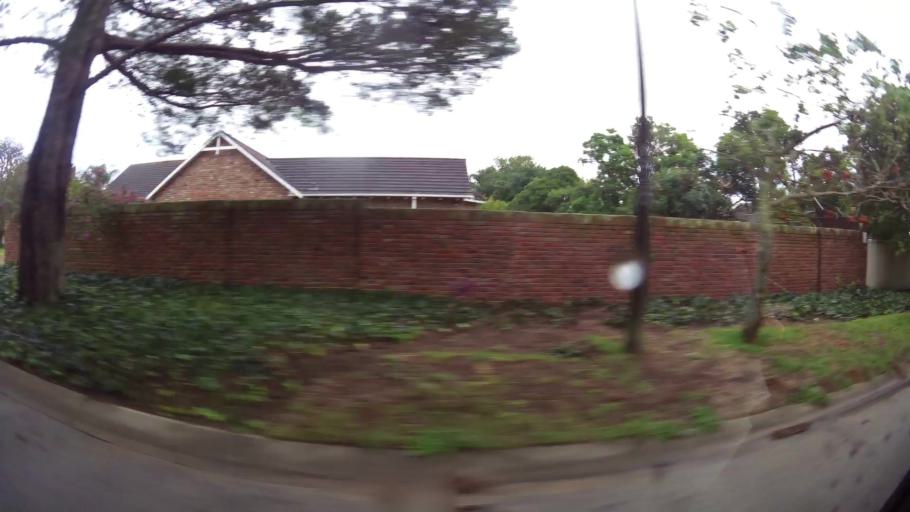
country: ZA
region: Eastern Cape
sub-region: Nelson Mandela Bay Metropolitan Municipality
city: Port Elizabeth
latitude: -33.9759
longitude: 25.5691
